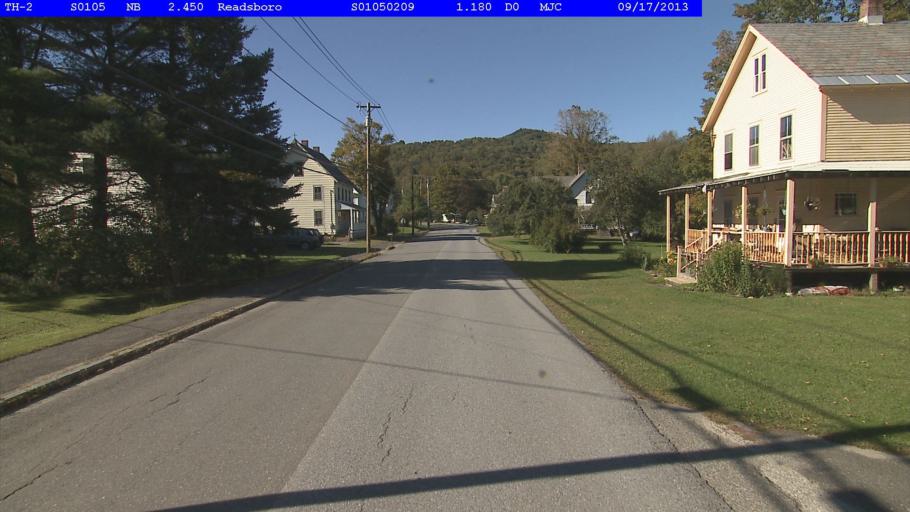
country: US
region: Massachusetts
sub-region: Franklin County
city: Charlemont
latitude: 42.7666
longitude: -72.9457
